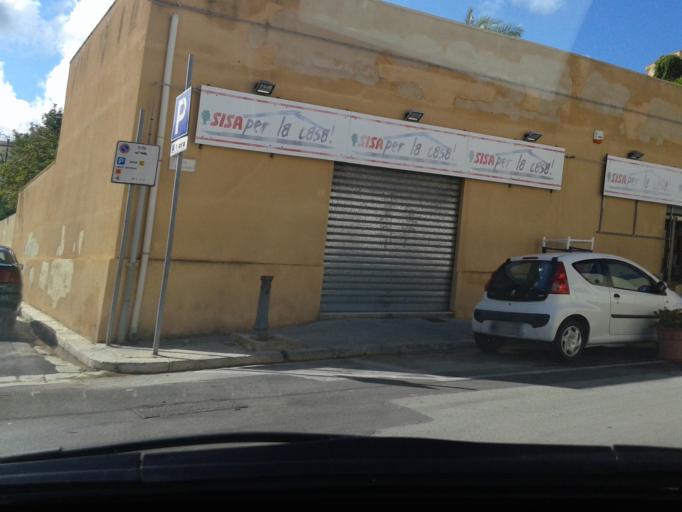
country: IT
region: Sicily
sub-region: Trapani
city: San Vito Lo Capo
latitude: 38.1724
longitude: 12.7345
